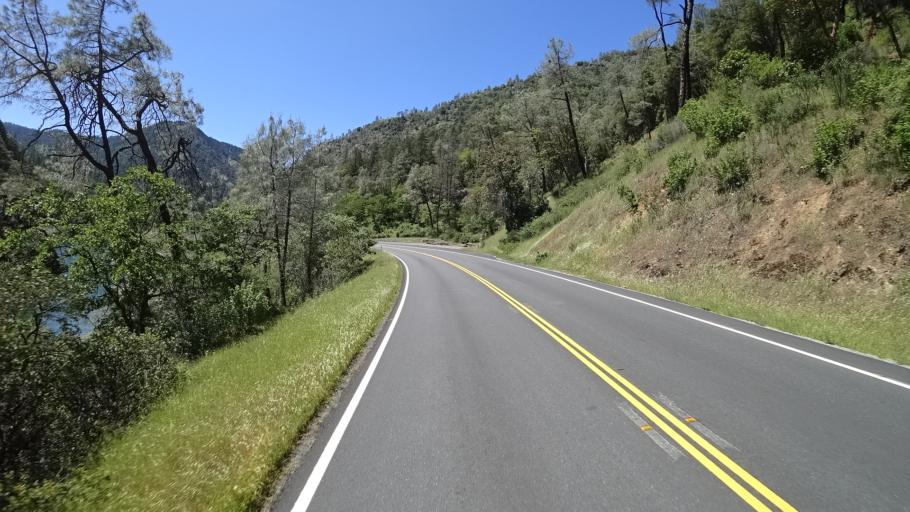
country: US
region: California
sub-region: Humboldt County
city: Willow Creek
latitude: 40.7907
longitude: -123.4350
